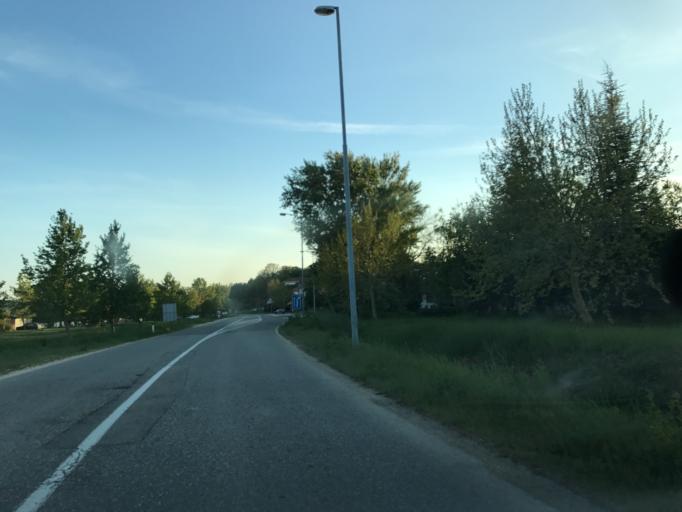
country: RO
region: Mehedinti
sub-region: Comuna Gogosu
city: Ostrovu Mare
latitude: 44.4838
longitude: 22.4561
